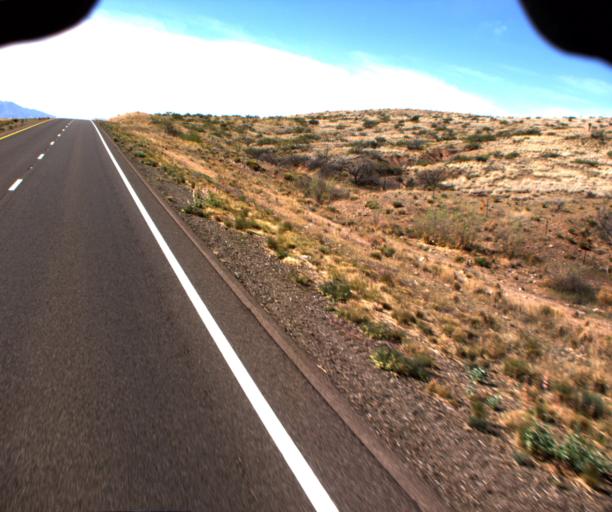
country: US
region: Arizona
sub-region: Cochise County
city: Willcox
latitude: 32.4308
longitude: -109.6635
